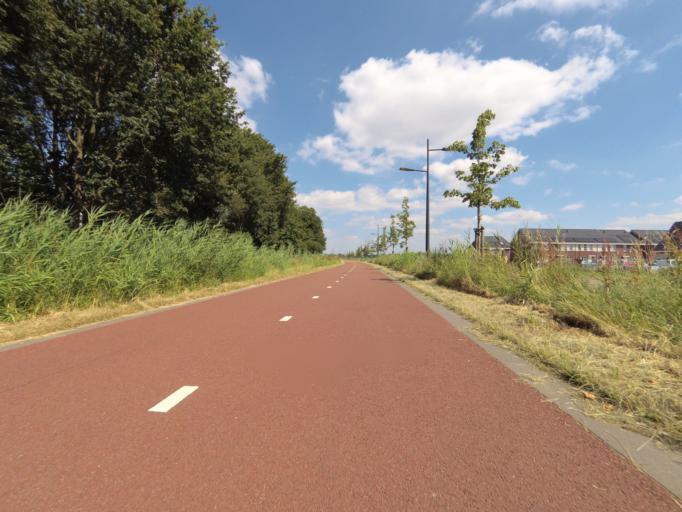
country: NL
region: Overijssel
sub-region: Gemeente Wierden
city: Wierden
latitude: 52.3525
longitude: 6.5947
